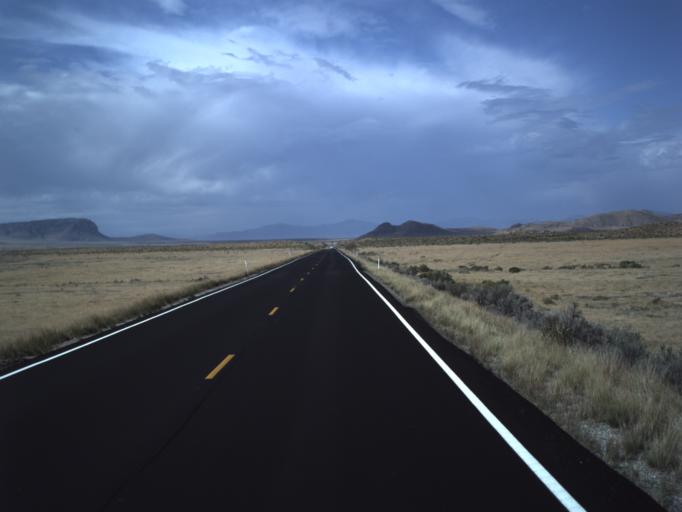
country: US
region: Utah
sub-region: Tooele County
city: Wendover
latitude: 41.4123
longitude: -113.9251
